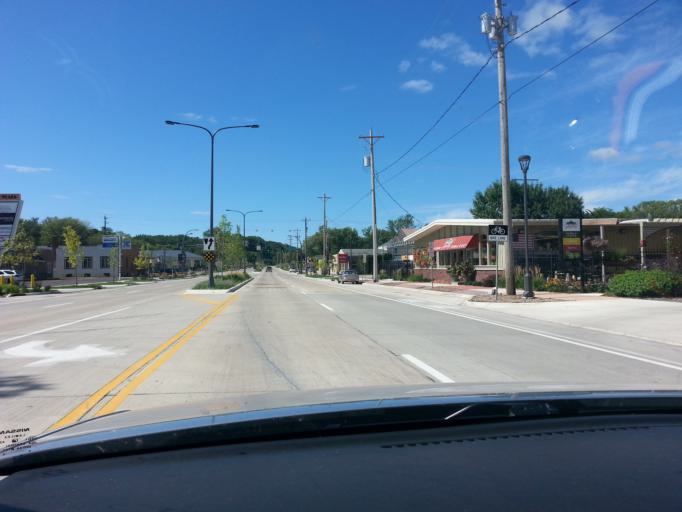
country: US
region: Minnesota
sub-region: Olmsted County
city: Rochester
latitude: 44.0217
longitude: -92.4907
